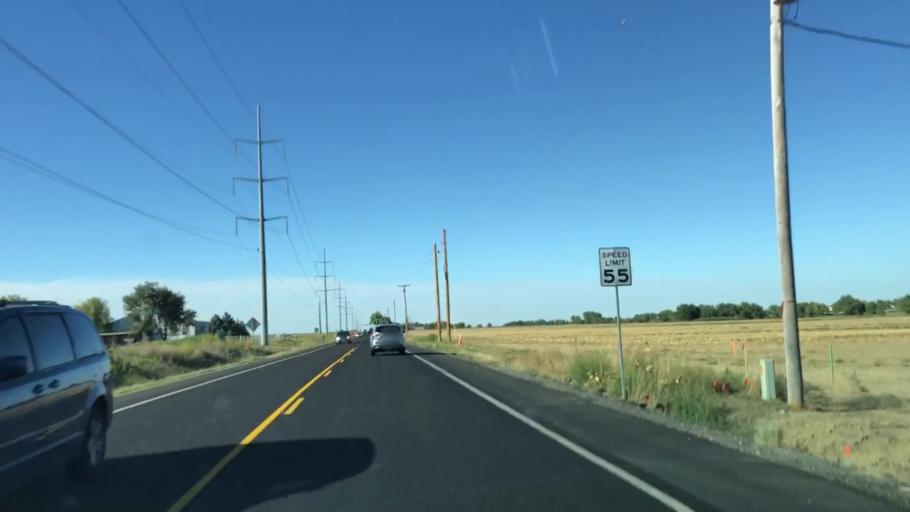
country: US
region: Colorado
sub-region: Larimer County
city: Loveland
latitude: 40.4515
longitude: -105.0442
